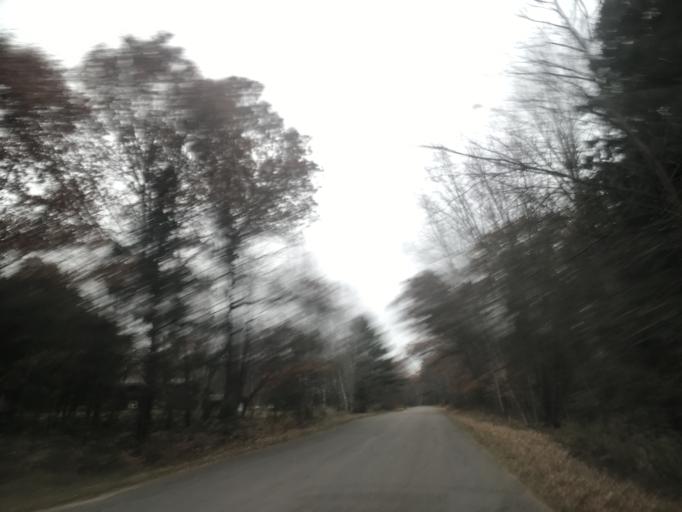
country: US
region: Michigan
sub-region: Dickinson County
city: Kingsford
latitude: 45.3810
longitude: -88.3214
